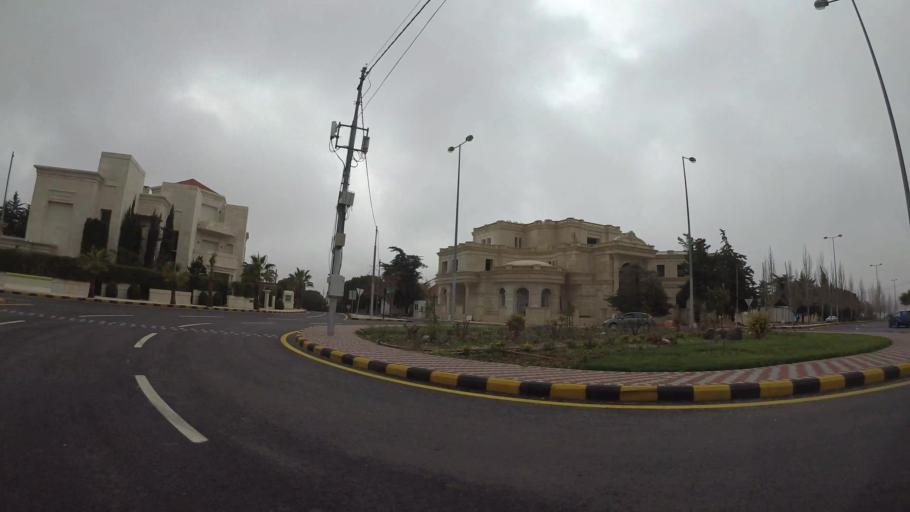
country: JO
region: Amman
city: Al Bunayyat ash Shamaliyah
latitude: 31.9375
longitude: 35.8783
